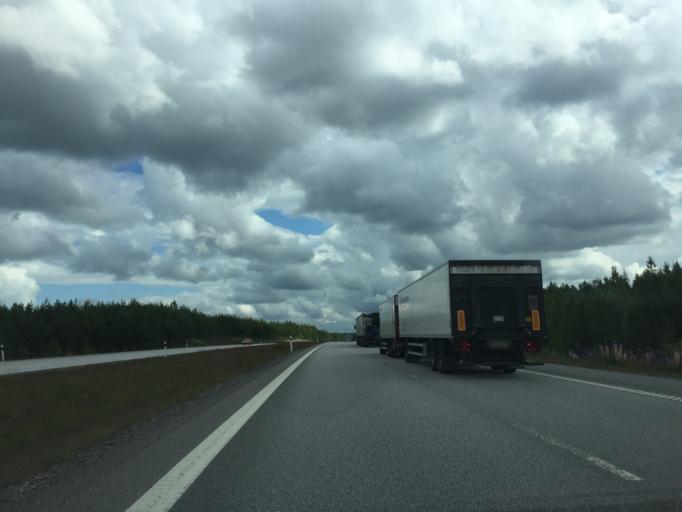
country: SE
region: OErebro
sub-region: Lindesbergs Kommun
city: Fellingsbro
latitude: 59.3760
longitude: 15.6090
